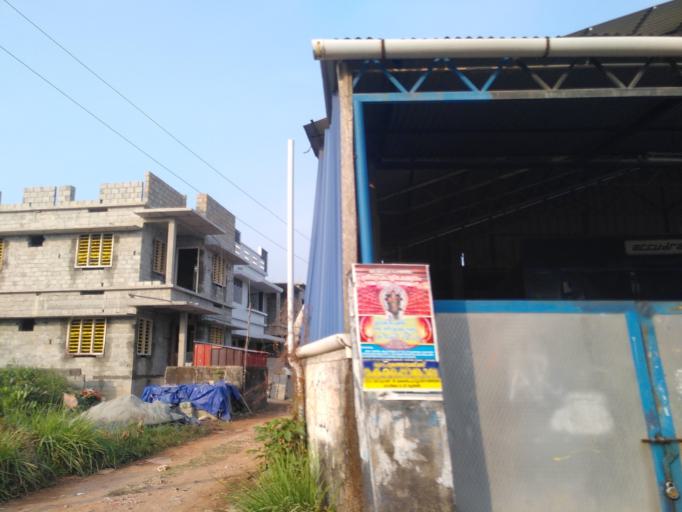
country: IN
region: Kerala
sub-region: Alappuzha
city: Arukutti
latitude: 9.9265
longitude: 76.3282
